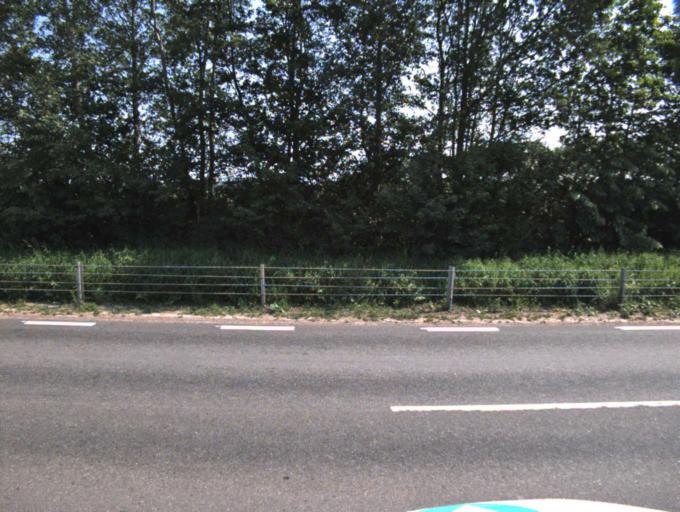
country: SE
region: Skane
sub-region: Kristianstads Kommun
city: Fjalkinge
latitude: 56.0774
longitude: 14.2209
